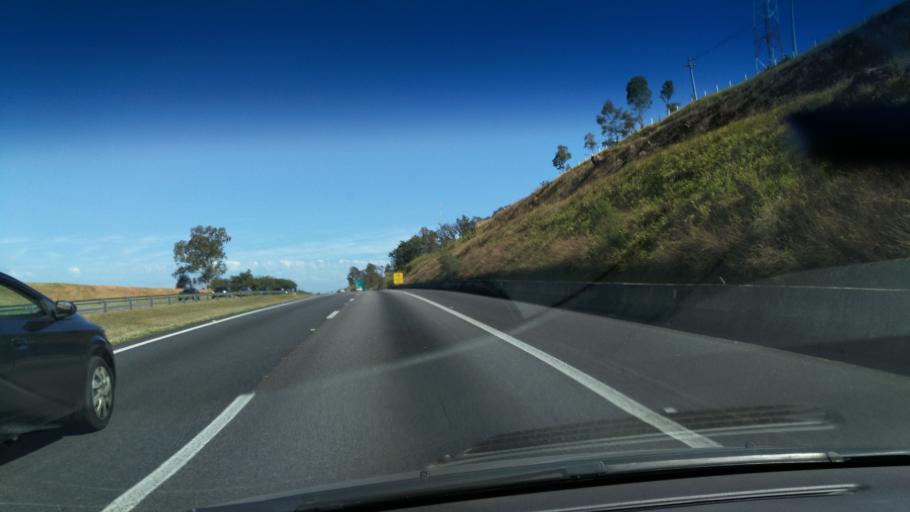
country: BR
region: Sao Paulo
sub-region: Valinhos
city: Valinhos
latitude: -22.9427
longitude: -47.0137
